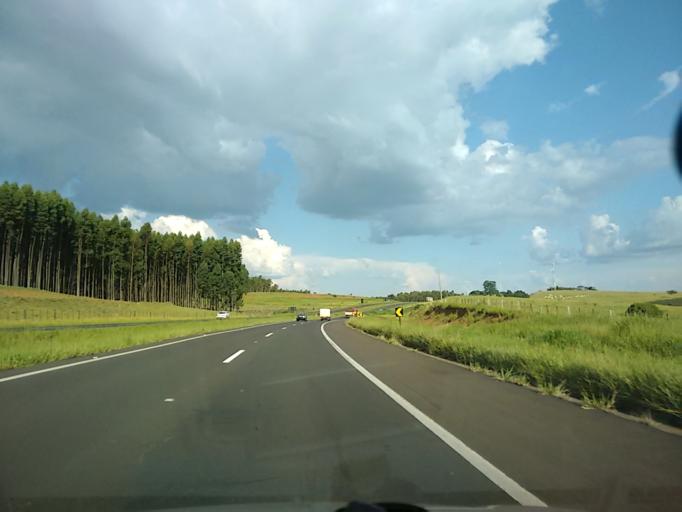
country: BR
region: Sao Paulo
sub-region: Duartina
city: Duartina
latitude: -22.3245
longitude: -49.3970
